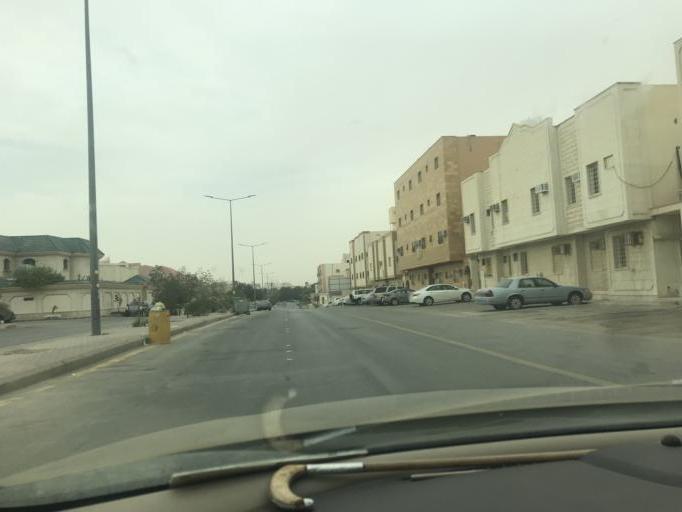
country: SA
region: Ar Riyad
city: Riyadh
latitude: 24.7362
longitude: 46.7573
